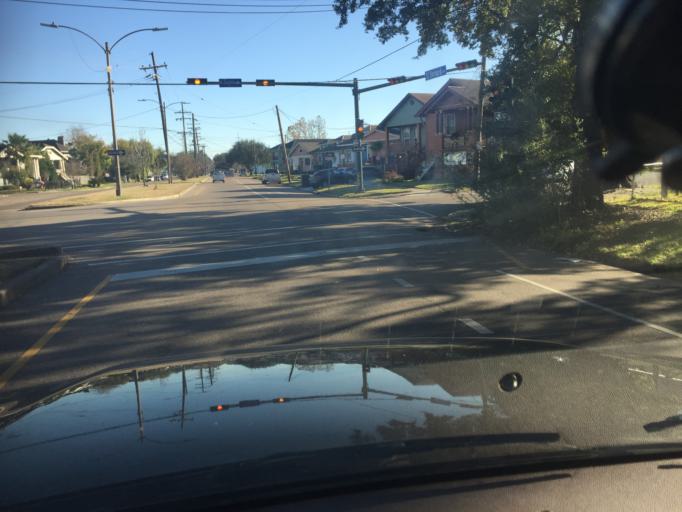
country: US
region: Louisiana
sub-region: Orleans Parish
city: New Orleans
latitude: 29.9855
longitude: -90.0730
